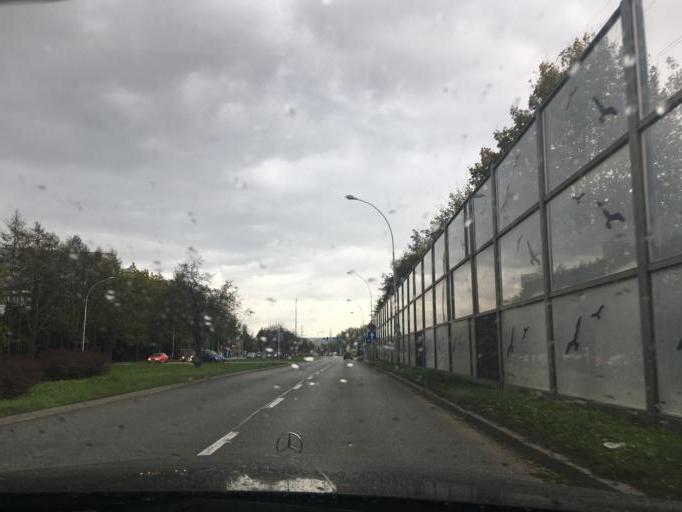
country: PL
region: Subcarpathian Voivodeship
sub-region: Rzeszow
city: Rzeszow
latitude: 50.0192
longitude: 22.0062
